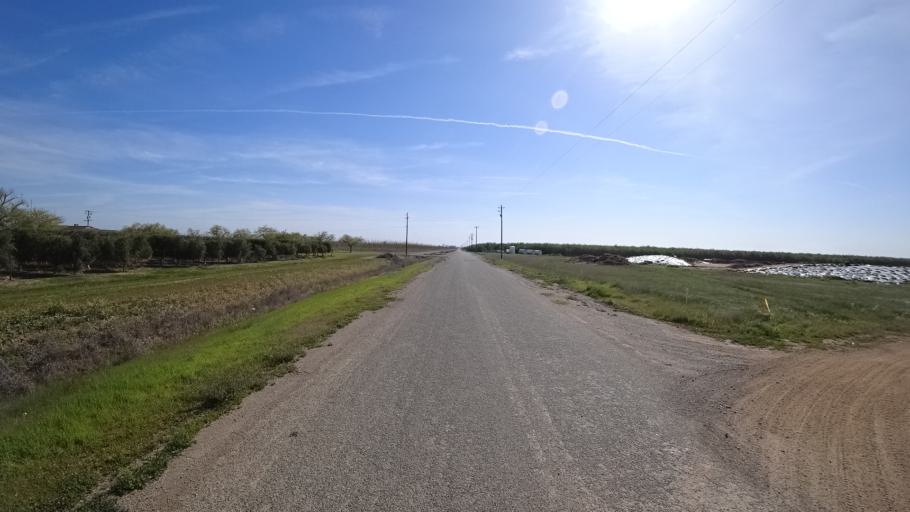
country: US
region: California
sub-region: Glenn County
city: Willows
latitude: 39.6114
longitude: -122.2245
